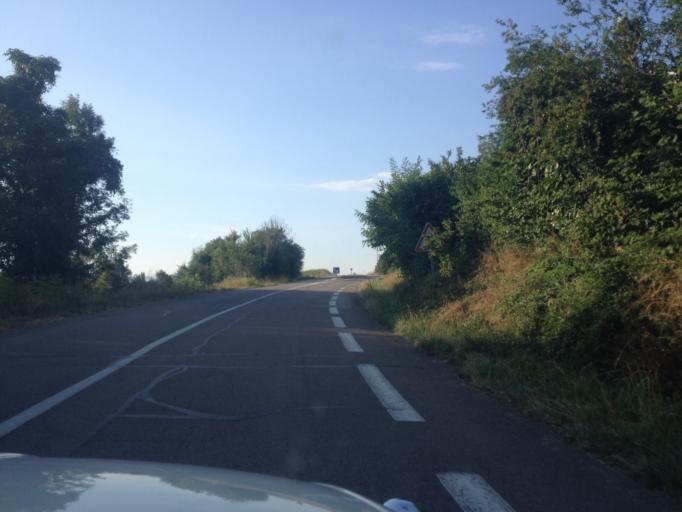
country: FR
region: Rhone-Alpes
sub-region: Departement de la Savoie
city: Drumettaz-Clarafond
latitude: 45.6652
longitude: 5.9390
